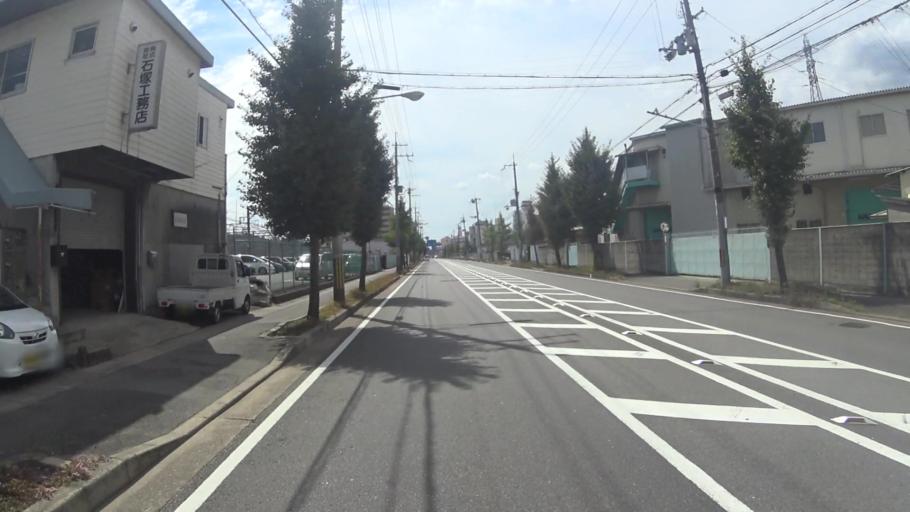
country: JP
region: Kyoto
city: Yawata
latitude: 34.8987
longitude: 135.7072
